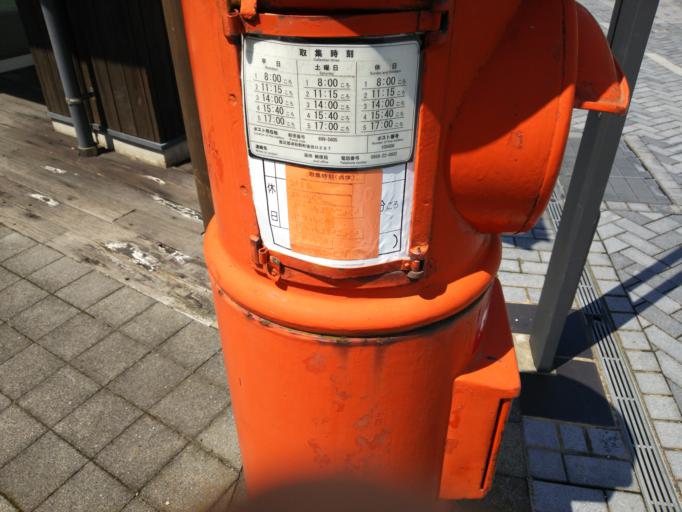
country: JP
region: Shimane
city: Masuda
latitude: 34.4708
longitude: 131.7756
